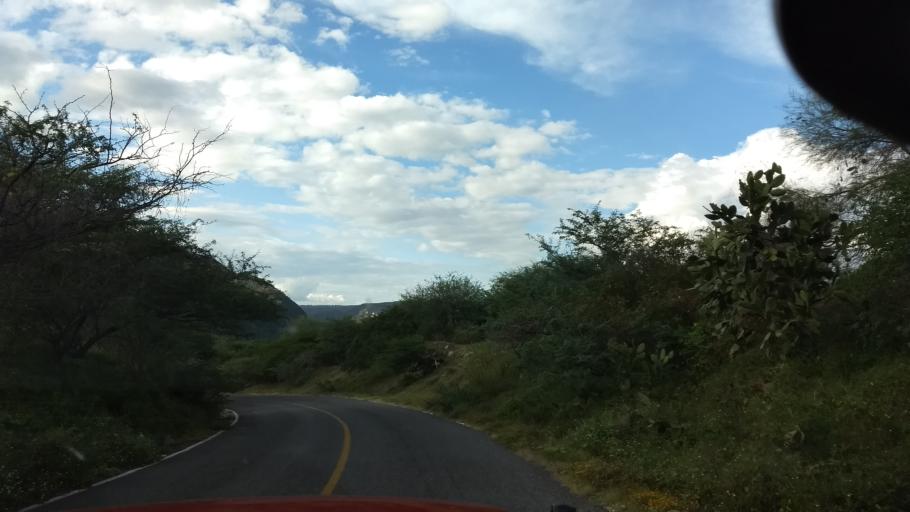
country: MX
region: Colima
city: Suchitlan
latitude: 19.4587
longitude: -103.8264
